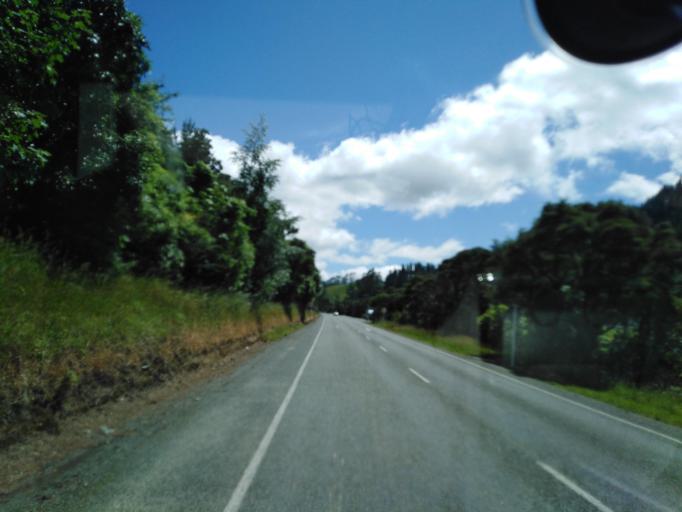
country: NZ
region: Nelson
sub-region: Nelson City
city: Nelson
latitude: -41.2243
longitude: 173.3963
